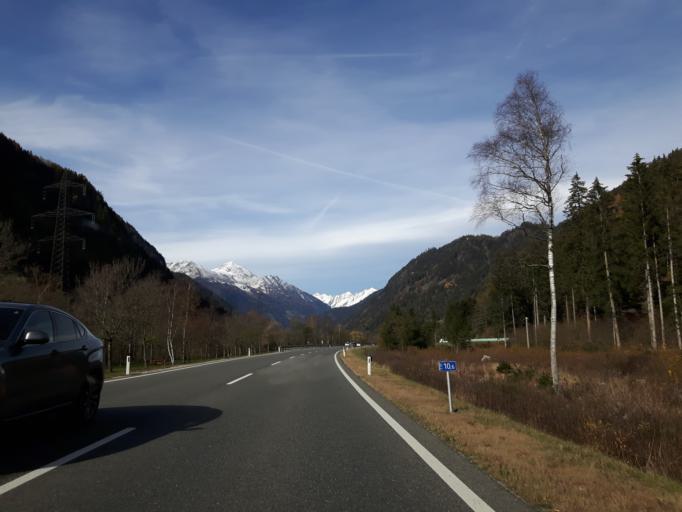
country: AT
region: Tyrol
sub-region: Politischer Bezirk Lienz
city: Schlaiten
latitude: 46.8928
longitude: 12.6492
